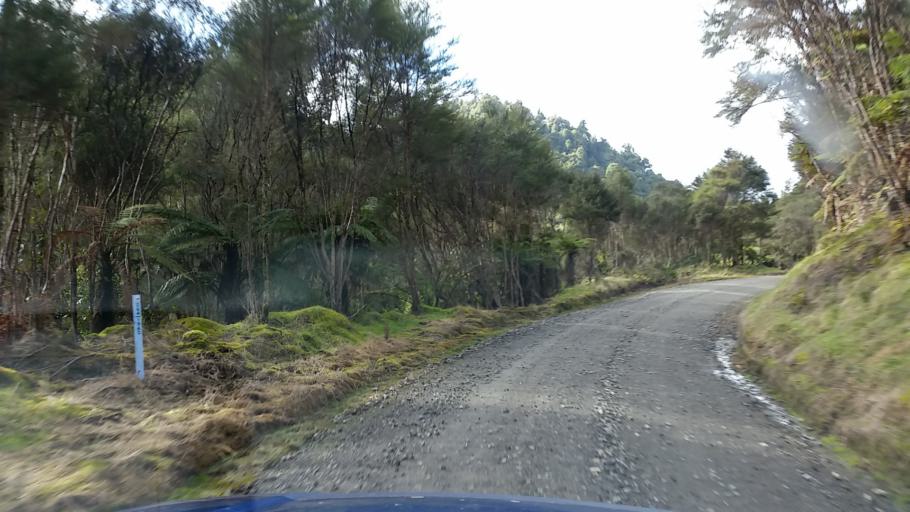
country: NZ
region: Taranaki
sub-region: South Taranaki District
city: Eltham
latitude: -39.2663
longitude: 174.7708
